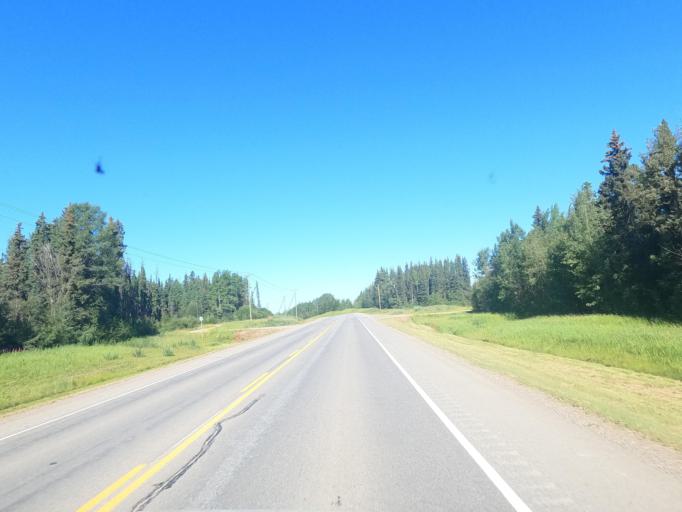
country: CA
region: British Columbia
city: Fort St. John
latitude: 56.6283
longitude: -121.5129
